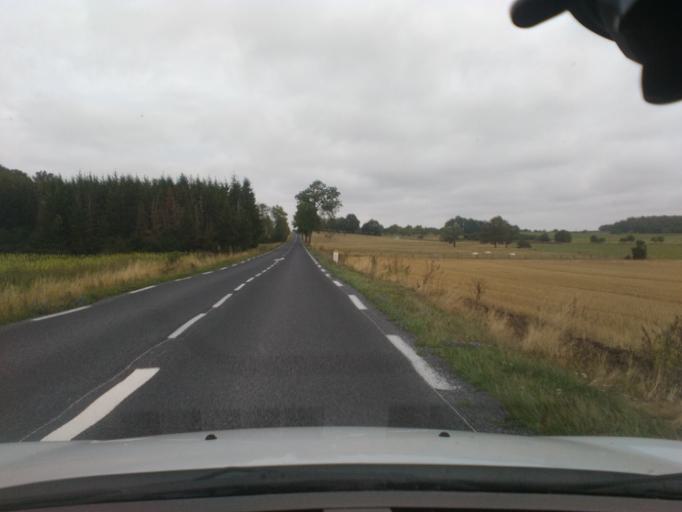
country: FR
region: Lorraine
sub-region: Departement de Meurthe-et-Moselle
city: Vezelise
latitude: 48.4094
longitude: 6.1359
